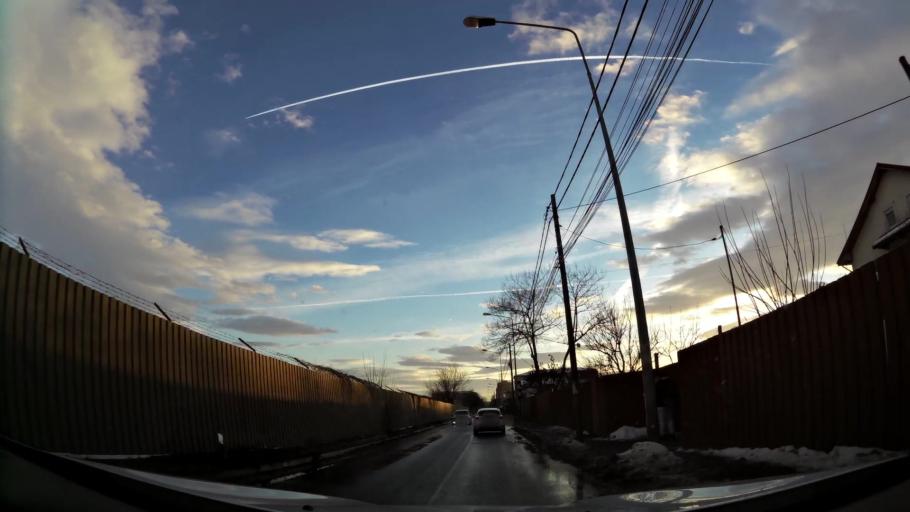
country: RO
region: Ilfov
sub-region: Comuna Popesti-Leordeni
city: Popesti-Leordeni
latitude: 44.3800
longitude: 26.1485
